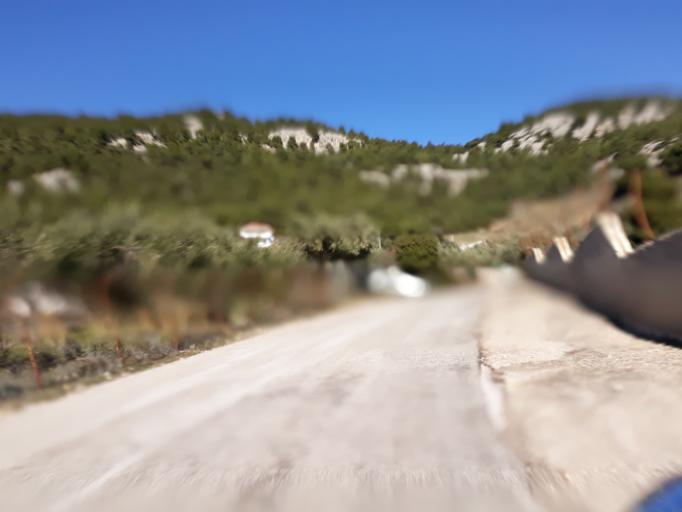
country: GR
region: Attica
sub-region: Nomarchia Dytikis Attikis
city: Fyli
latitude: 38.1133
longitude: 23.6748
